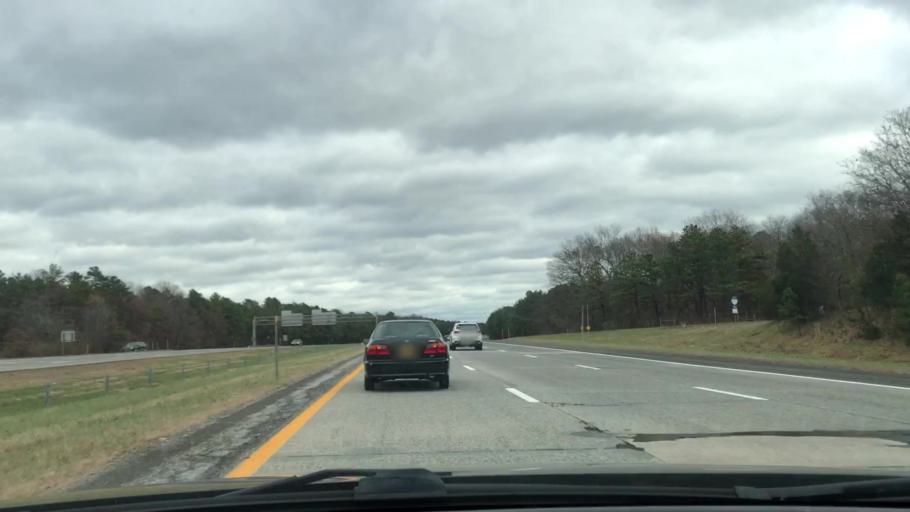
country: US
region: New York
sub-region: Suffolk County
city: Manorville
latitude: 40.8725
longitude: -72.7998
